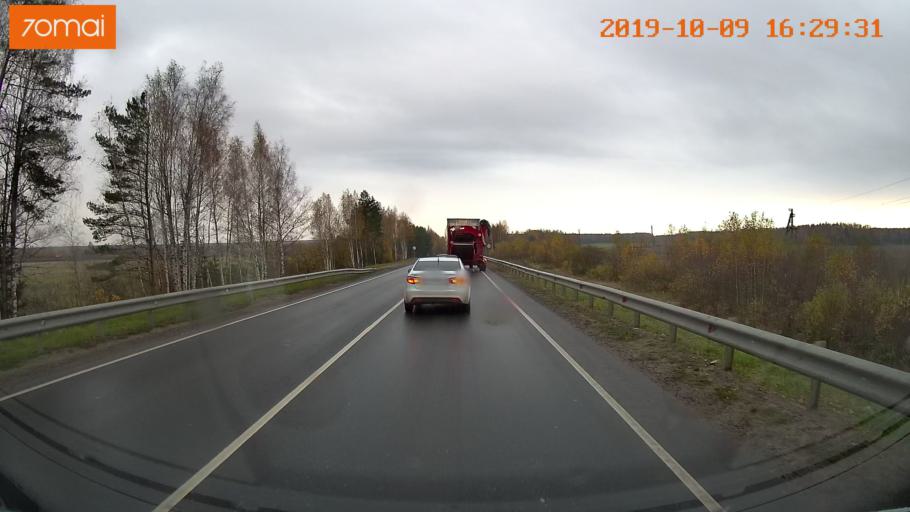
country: RU
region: Kostroma
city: Oktyabr'skiy
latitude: 57.6239
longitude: 40.9367
